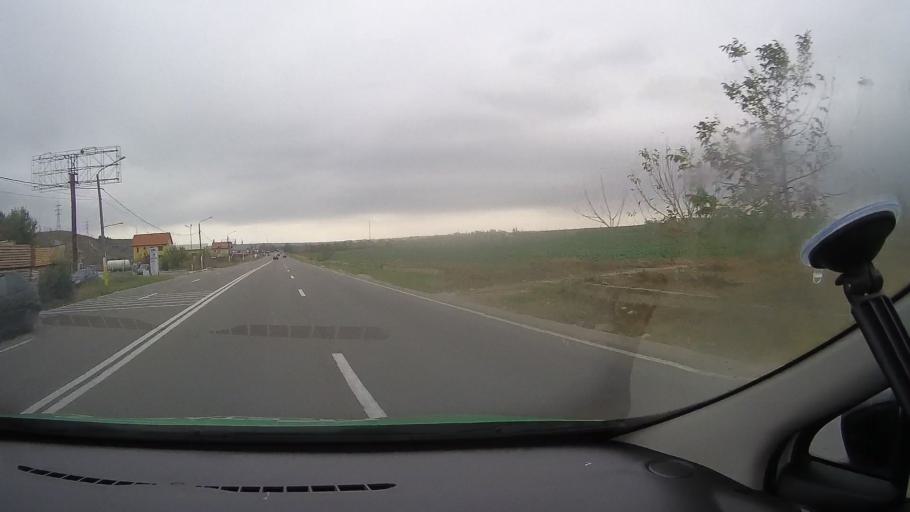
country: RO
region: Constanta
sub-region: Oras Murfatlar
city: Murfatlar
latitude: 44.1699
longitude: 28.4371
